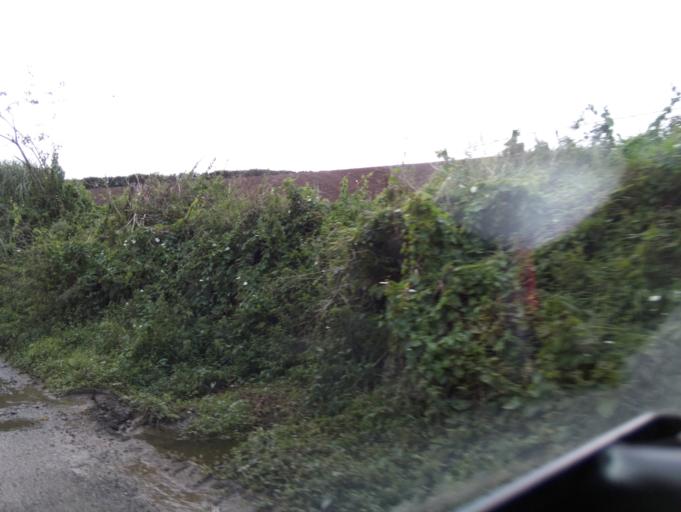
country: GB
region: England
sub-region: Devon
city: Kingsbridge
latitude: 50.2797
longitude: -3.8118
